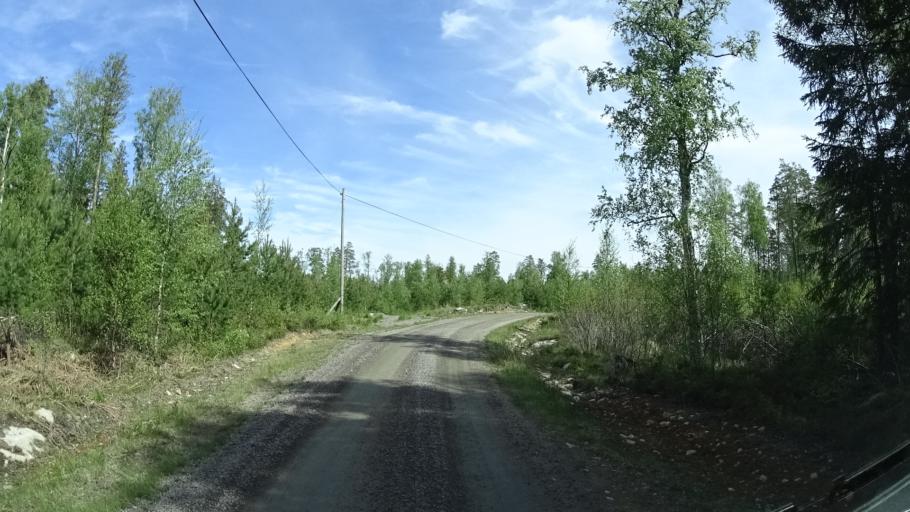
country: SE
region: OEstergoetland
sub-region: Finspangs Kommun
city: Finspang
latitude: 58.7772
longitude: 15.8533
